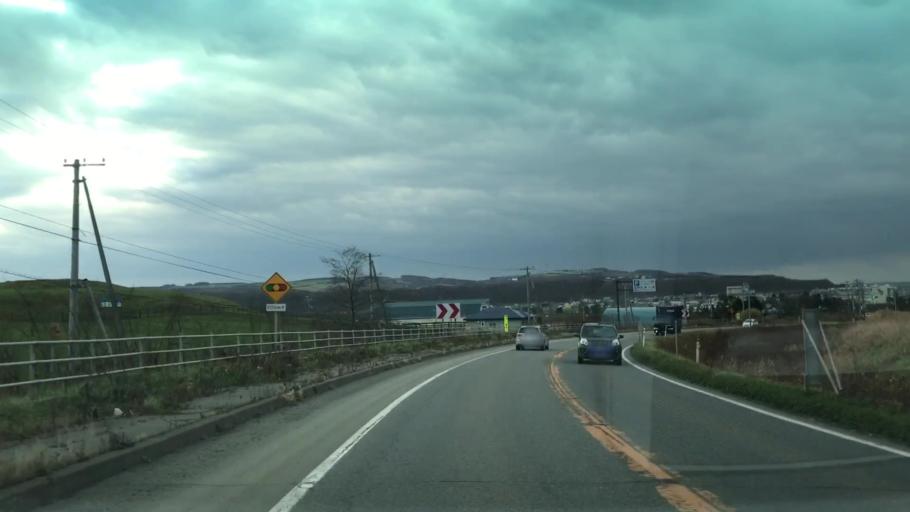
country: JP
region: Hokkaido
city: Shizunai-furukawacho
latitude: 42.3748
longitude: 142.3079
